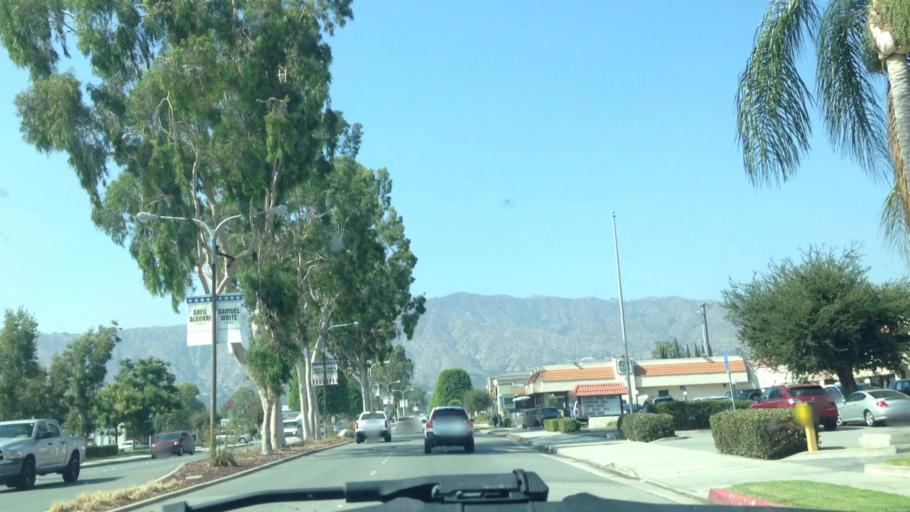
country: US
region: California
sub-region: Los Angeles County
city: Glendora
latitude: 34.1254
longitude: -117.8726
